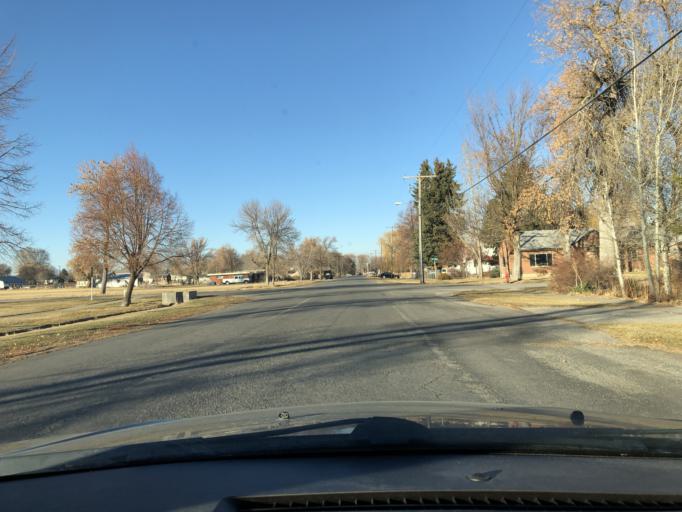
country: US
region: Utah
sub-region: Cache County
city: Wellsville
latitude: 41.6404
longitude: -111.9315
